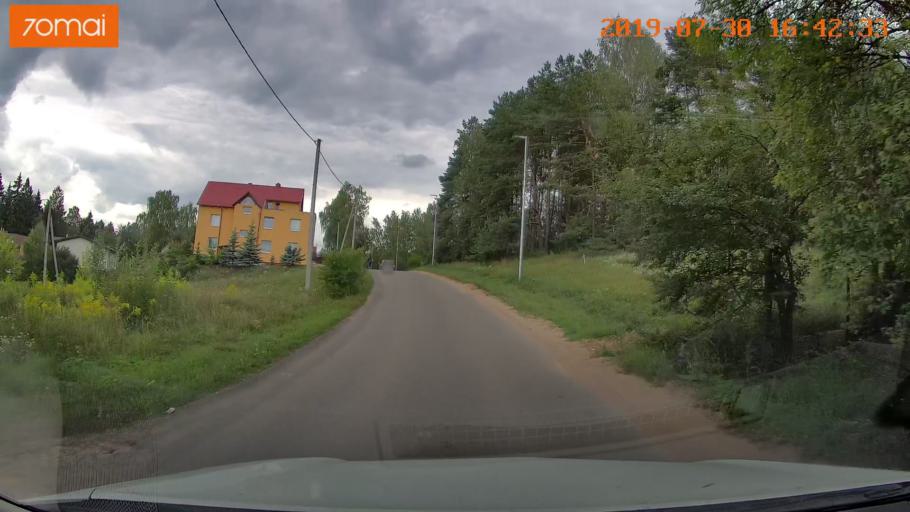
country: LT
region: Vilnius County
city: Rasos
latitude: 54.7164
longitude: 25.3536
